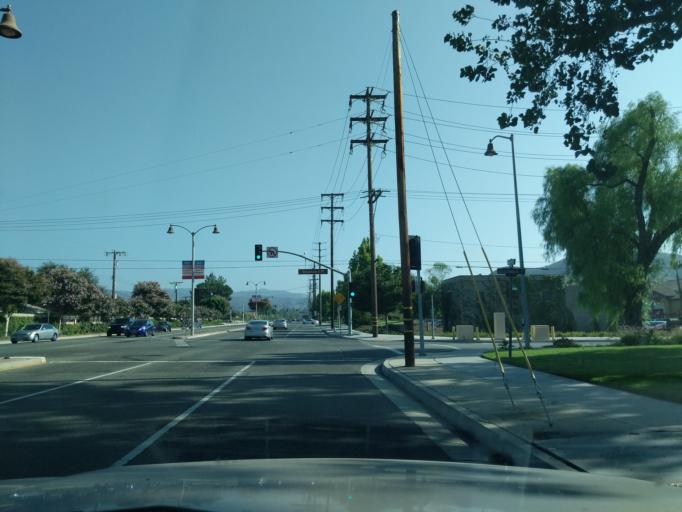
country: US
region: California
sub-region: Ventura County
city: Simi Valley
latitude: 34.2743
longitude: -118.7965
